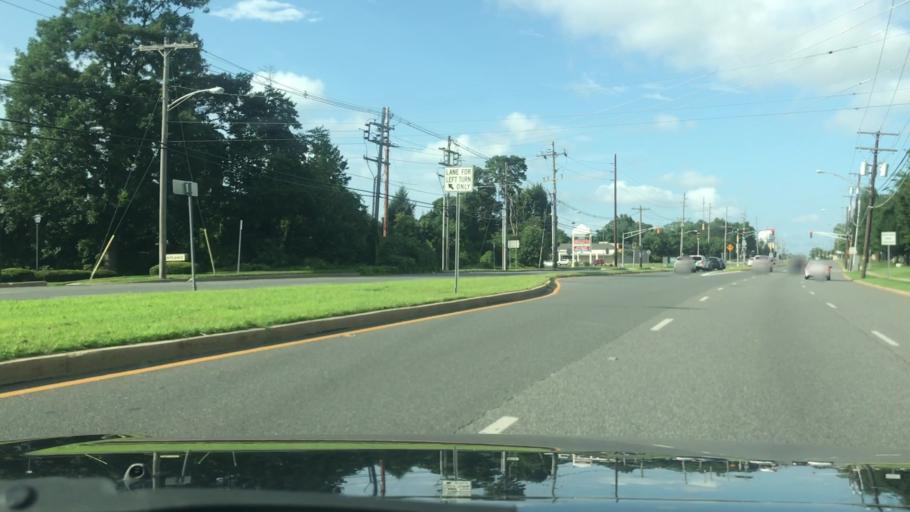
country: US
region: New Jersey
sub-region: Ocean County
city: Toms River
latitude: 39.9880
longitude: -74.1775
